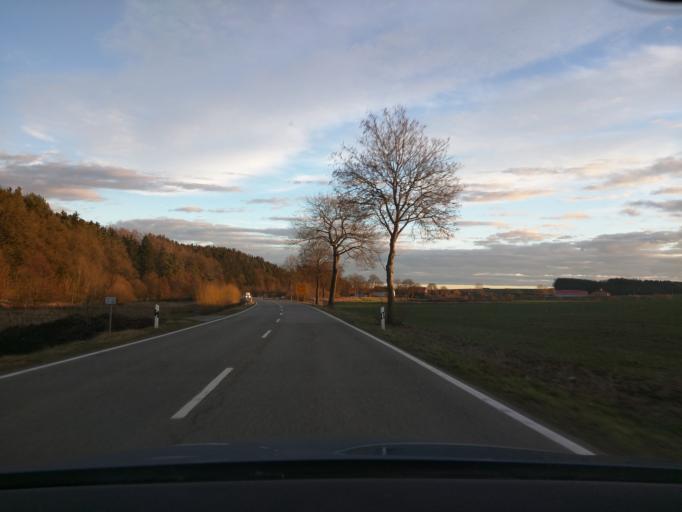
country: DE
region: Bavaria
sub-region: Upper Bavaria
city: Zolling
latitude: 48.4736
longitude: 11.7608
